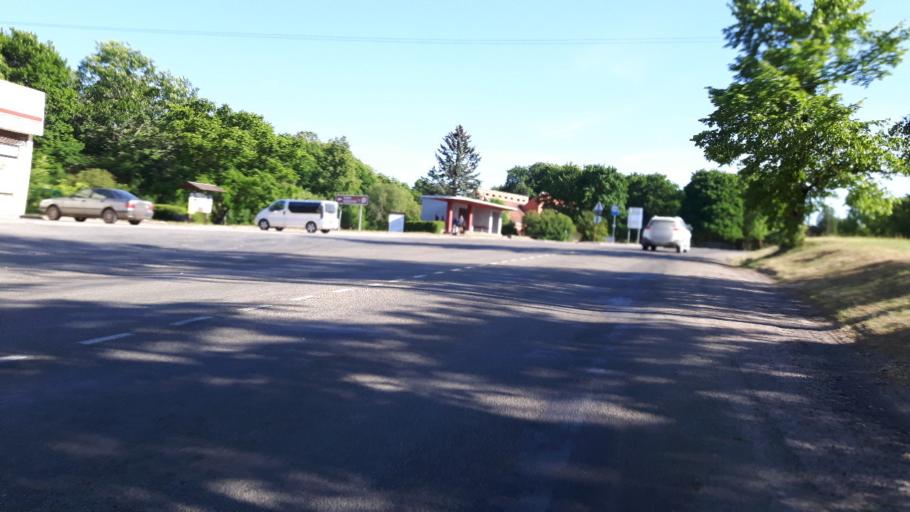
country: LV
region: Talsu Rajons
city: Stende
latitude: 57.0687
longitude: 22.2935
